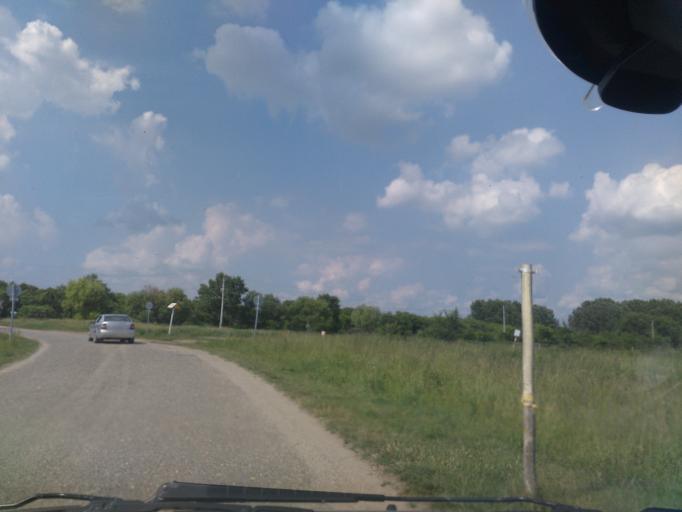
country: HU
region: Pest
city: Veresegyhaz
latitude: 47.6374
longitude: 19.2610
